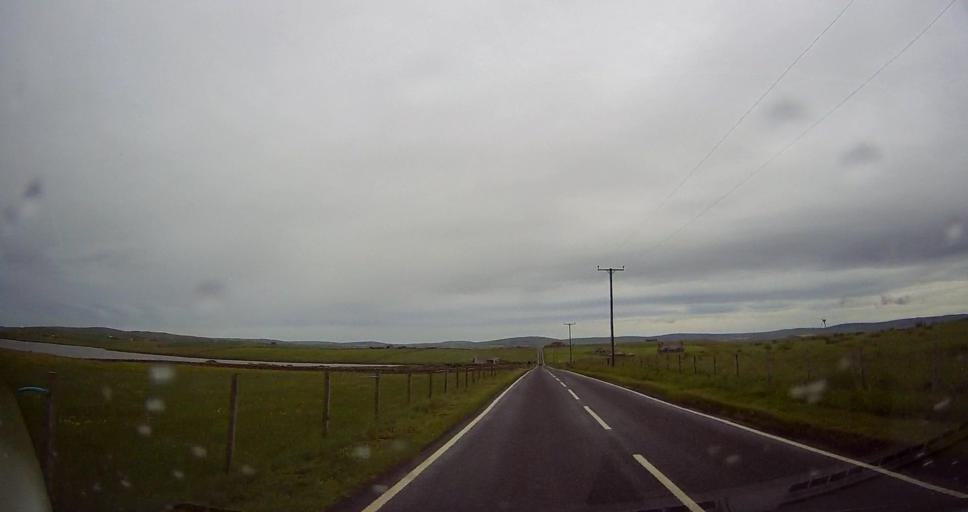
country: GB
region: Scotland
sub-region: Orkney Islands
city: Stromness
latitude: 59.0224
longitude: -3.2968
